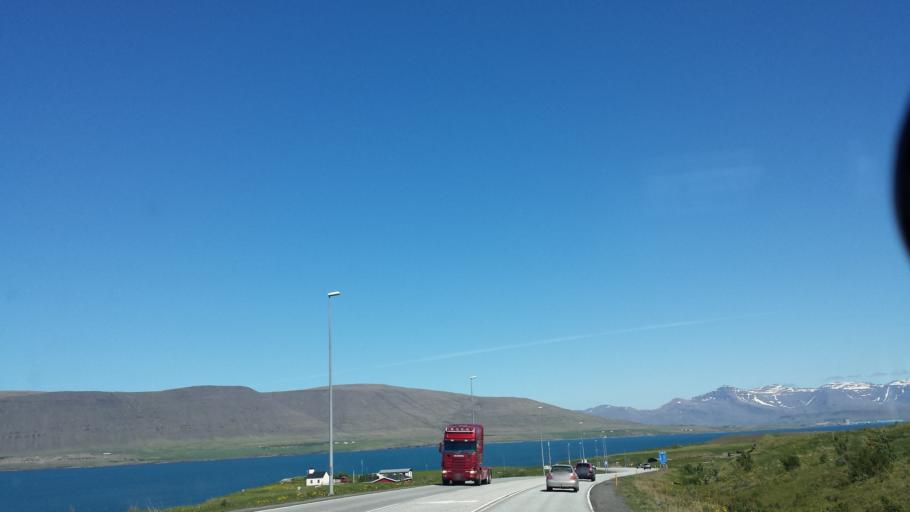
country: IS
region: Capital Region
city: Reykjavik
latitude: 64.2772
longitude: -21.8405
